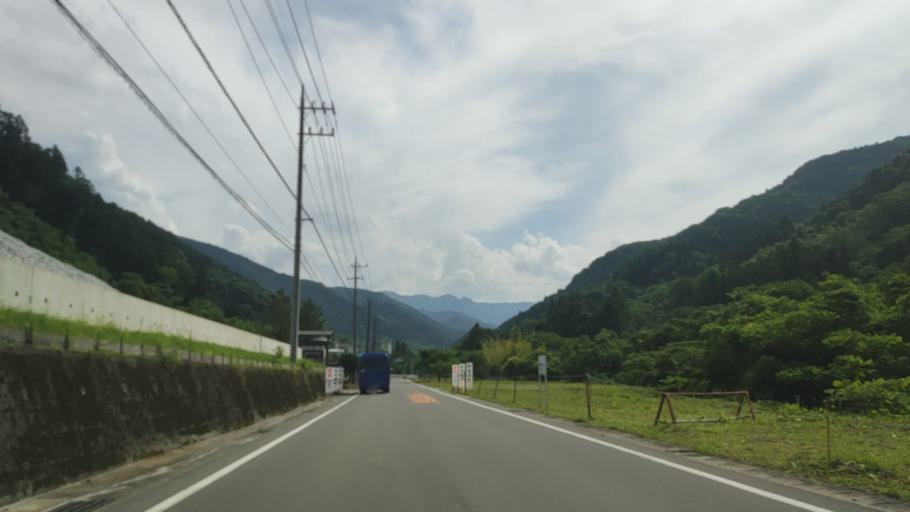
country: JP
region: Gunma
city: Tomioka
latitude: 36.1920
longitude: 138.7522
